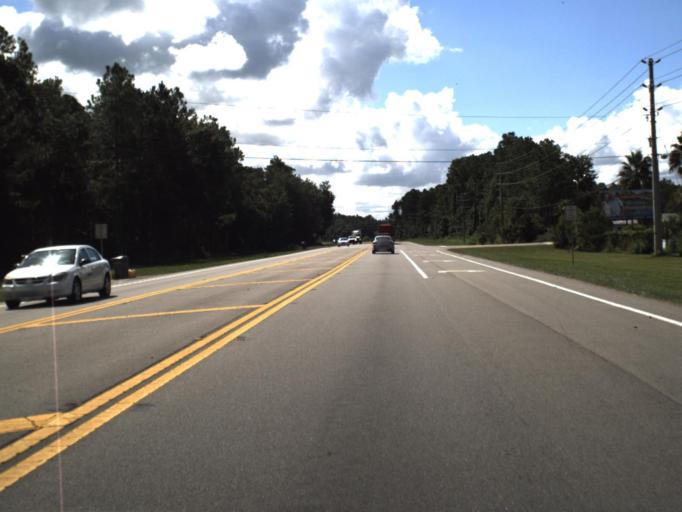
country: US
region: Florida
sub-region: Polk County
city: Kathleen
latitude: 28.1876
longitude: -81.9981
